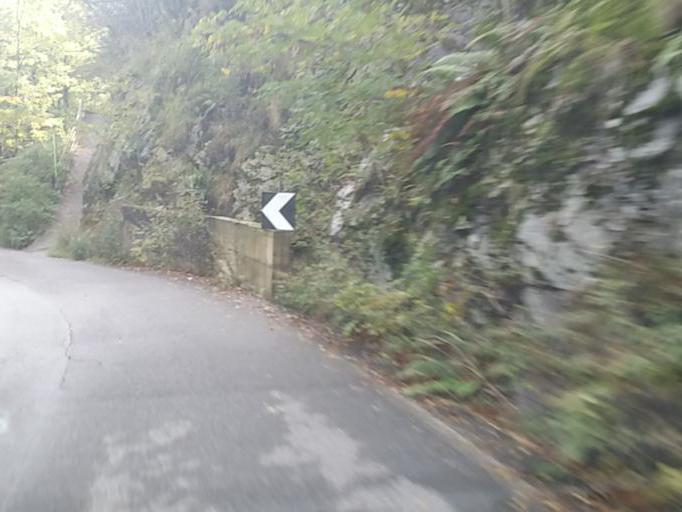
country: IT
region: Piedmont
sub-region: Provincia Verbano-Cusio-Ossola
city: Trarego
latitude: 46.0591
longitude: 8.6679
